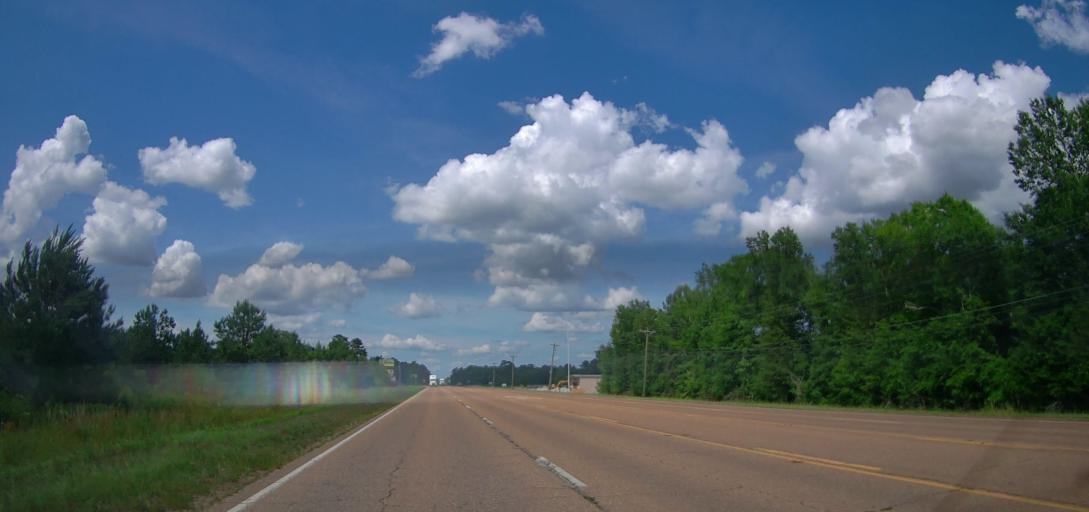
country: US
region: Mississippi
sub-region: Lowndes County
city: Columbus Air Force Base
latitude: 33.5743
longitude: -88.4304
